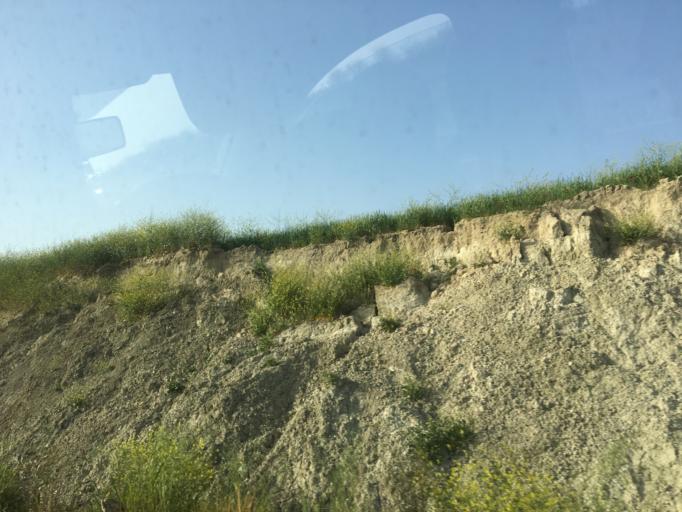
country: TR
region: Manisa
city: Ahmetli
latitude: 38.5665
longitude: 28.0346
